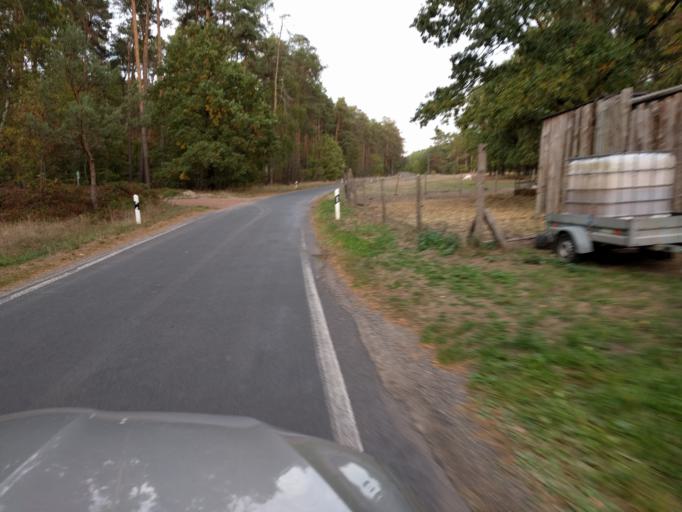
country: DE
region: Brandenburg
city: Ziesar
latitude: 52.2186
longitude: 12.2829
